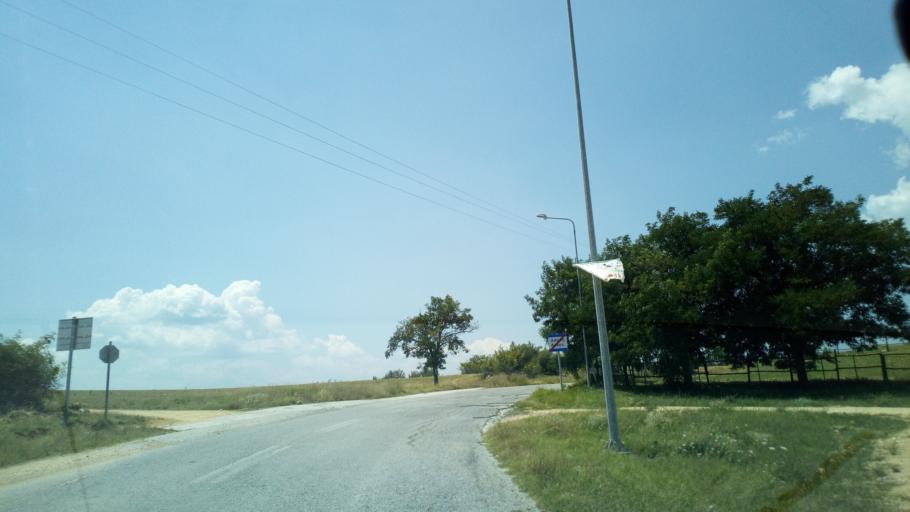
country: GR
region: Central Macedonia
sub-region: Nomos Thessalonikis
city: Askos
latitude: 40.7392
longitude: 23.3849
